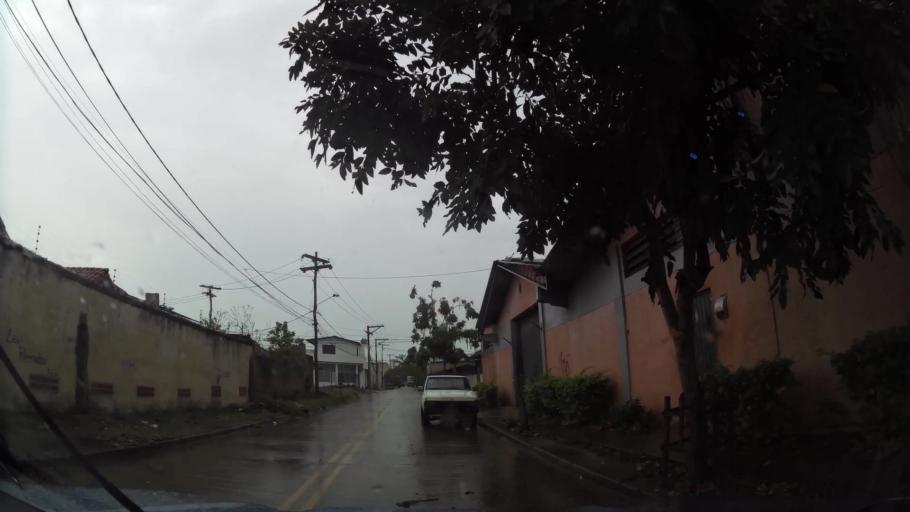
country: BO
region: Santa Cruz
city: Santa Cruz de la Sierra
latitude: -17.7846
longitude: -63.2024
